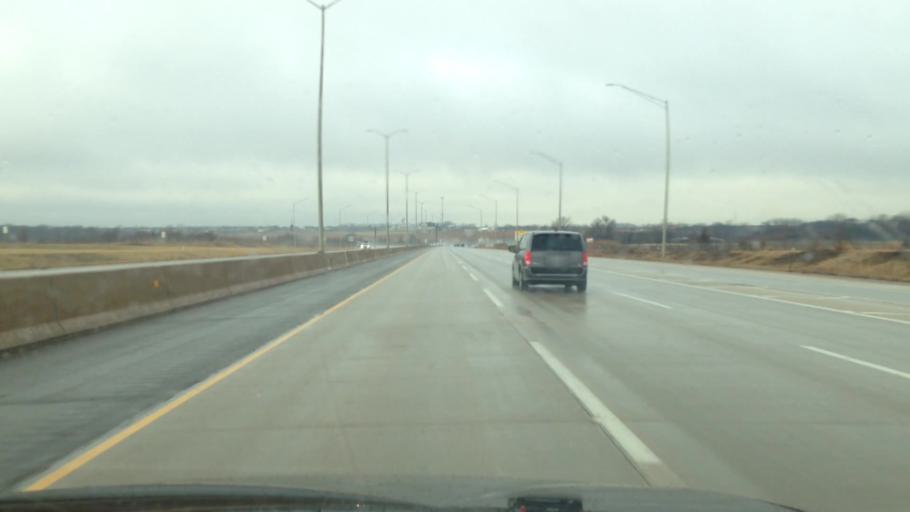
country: US
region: Illinois
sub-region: Will County
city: New Lenox
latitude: 41.5507
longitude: -87.9810
